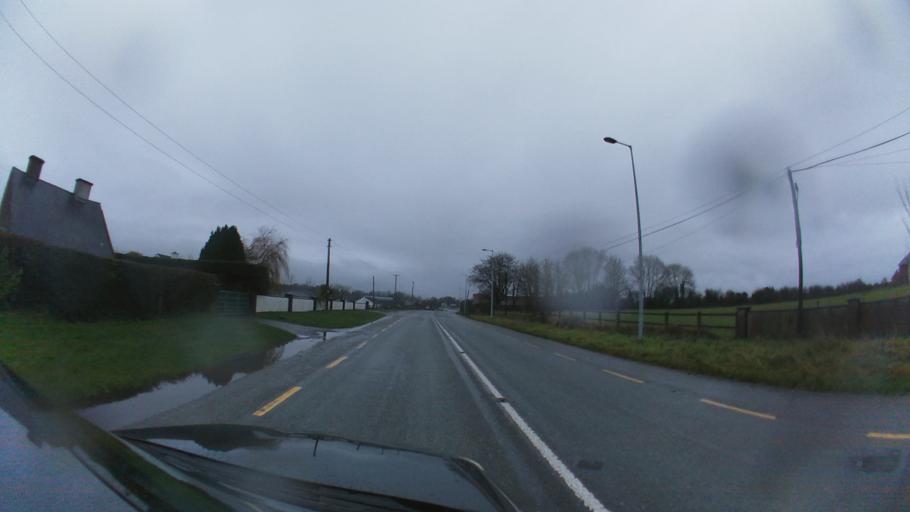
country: IE
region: Leinster
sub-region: County Carlow
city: Bagenalstown
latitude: 52.6747
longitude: -7.0244
